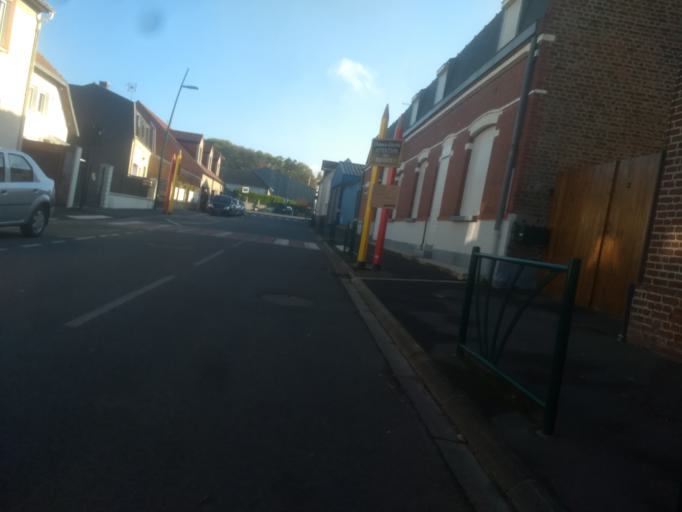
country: FR
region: Nord-Pas-de-Calais
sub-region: Departement du Pas-de-Calais
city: Tilloy-les-Mofflaines
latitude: 50.2751
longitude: 2.8155
